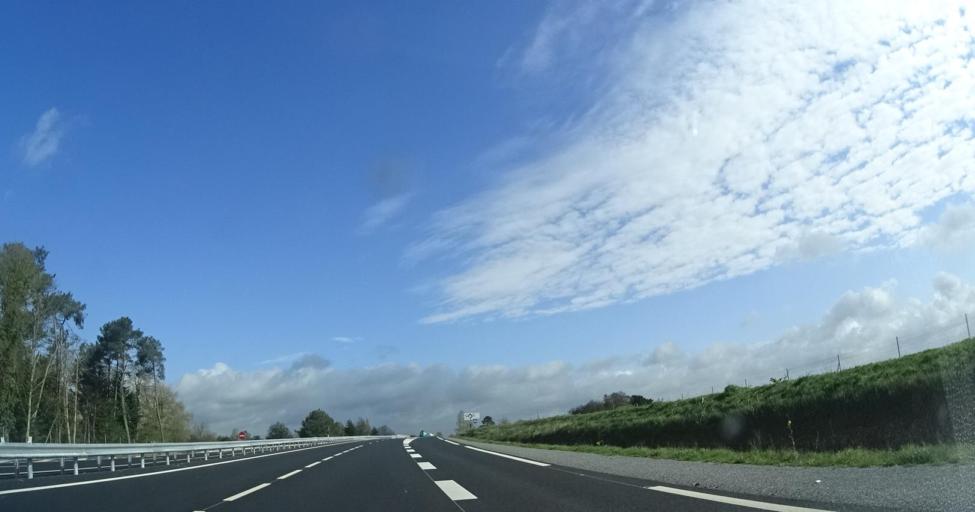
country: FR
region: Brittany
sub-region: Departement d'Ille-et-Vilaine
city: Pipriac
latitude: 47.8135
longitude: -1.9202
